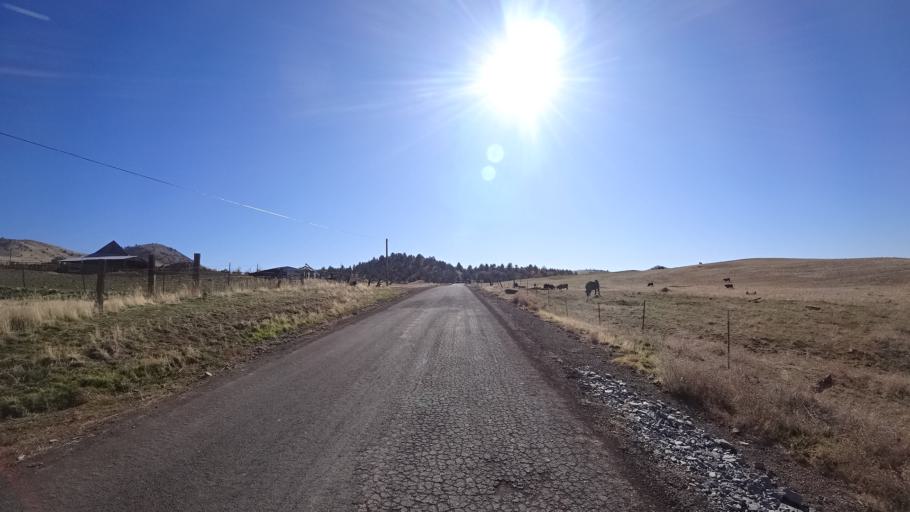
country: US
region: California
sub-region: Siskiyou County
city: Montague
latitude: 41.8117
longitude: -122.3760
